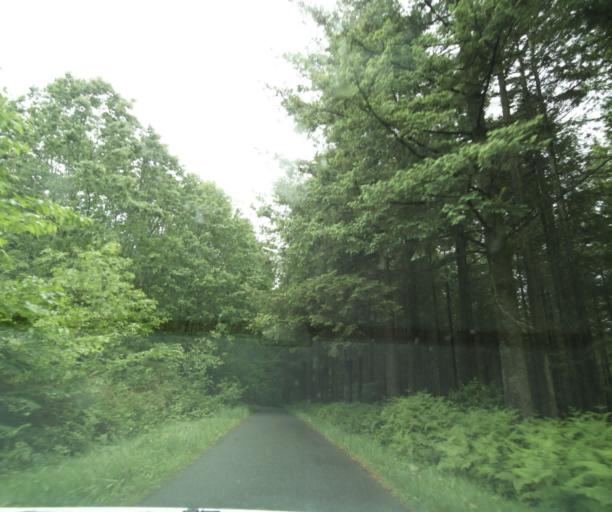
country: FR
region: Bourgogne
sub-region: Departement de Saone-et-Loire
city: Palinges
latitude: 46.5373
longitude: 4.2648
